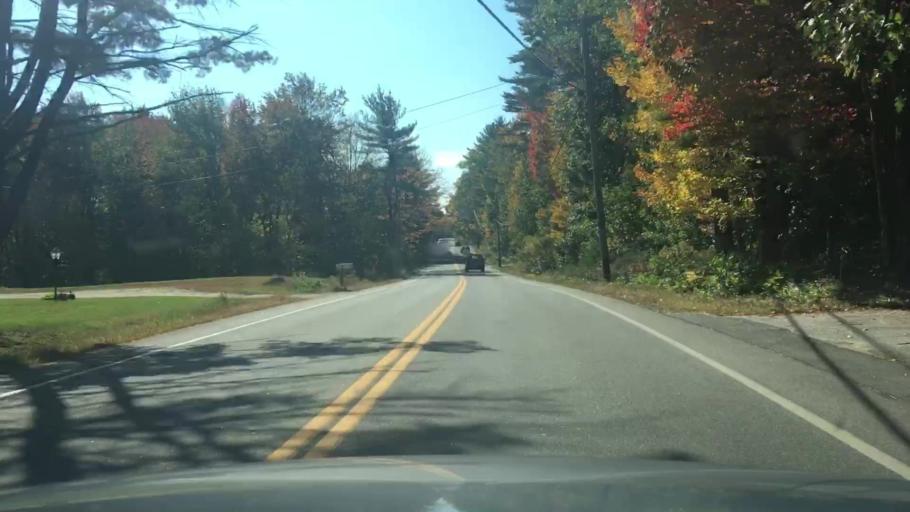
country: US
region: Maine
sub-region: Cumberland County
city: Gorham
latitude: 43.6346
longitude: -70.4417
